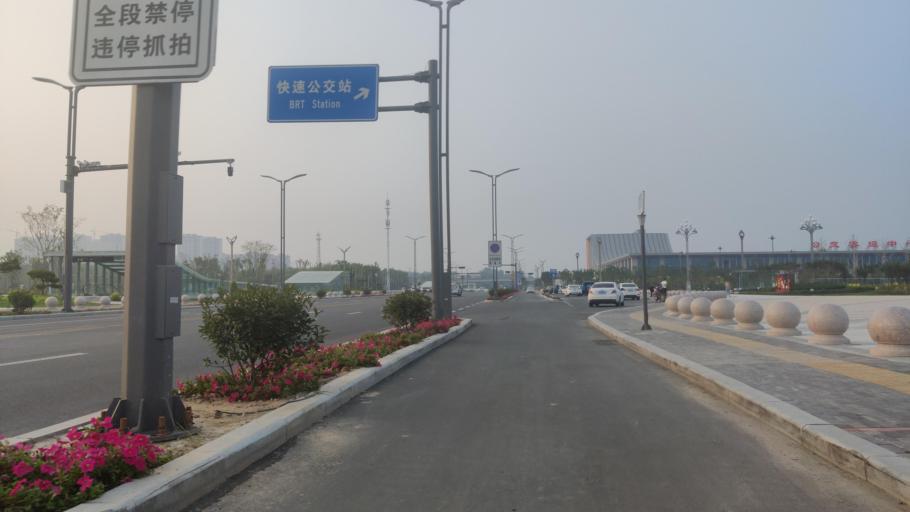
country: CN
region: Henan Sheng
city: Zhongyuanlu
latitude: 35.7643
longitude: 115.1404
